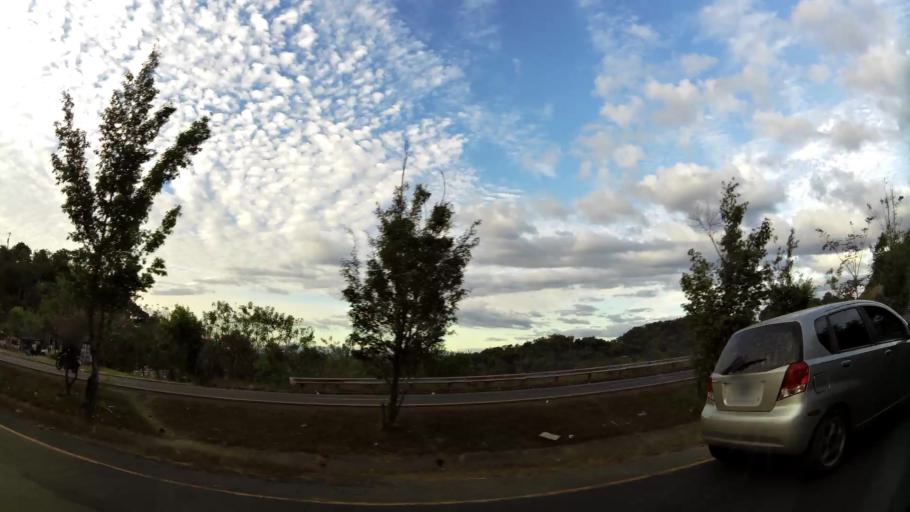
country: SV
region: Cuscatlan
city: Cojutepeque
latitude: 13.7238
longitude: -88.9036
